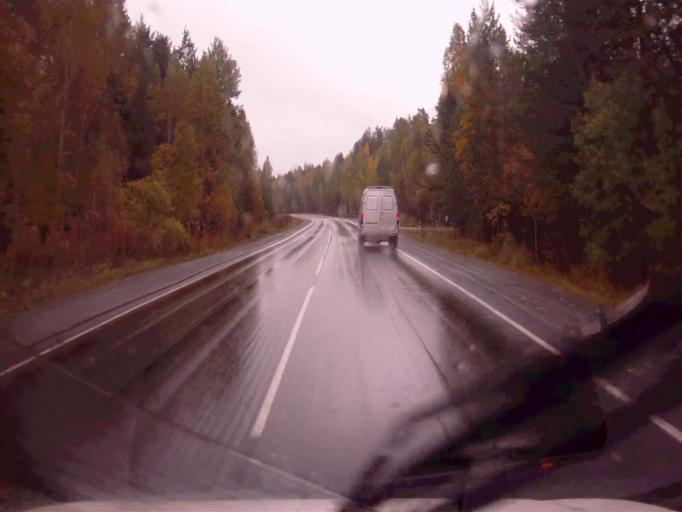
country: RU
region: Chelyabinsk
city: Tayginka
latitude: 55.5676
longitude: 60.6506
